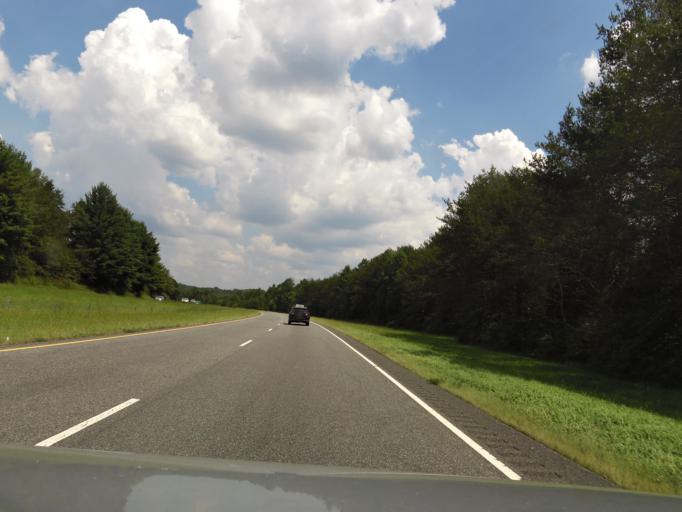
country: US
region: North Carolina
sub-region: Polk County
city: Columbus
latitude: 35.2721
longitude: -82.1391
